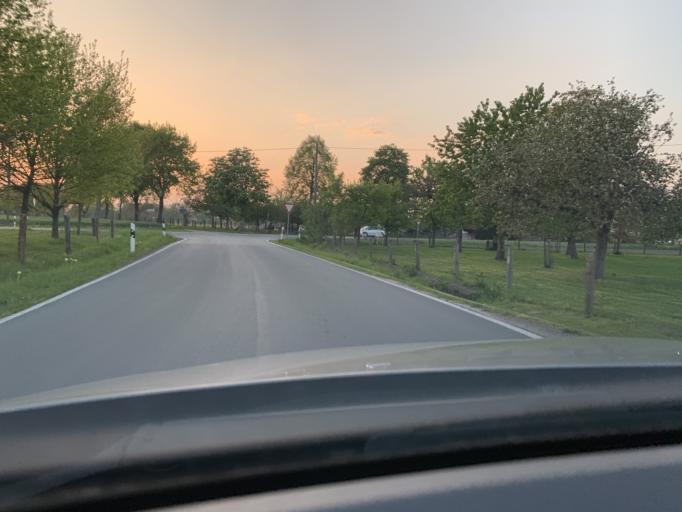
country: DE
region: North Rhine-Westphalia
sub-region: Regierungsbezirk Detmold
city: Langenberg
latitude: 51.7897
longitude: 8.3716
